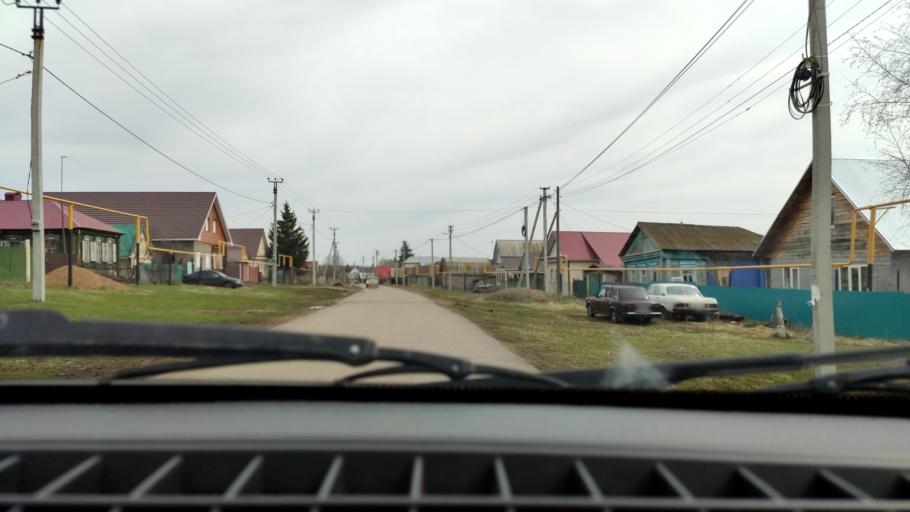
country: RU
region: Bashkortostan
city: Avdon
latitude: 54.6408
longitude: 55.7376
